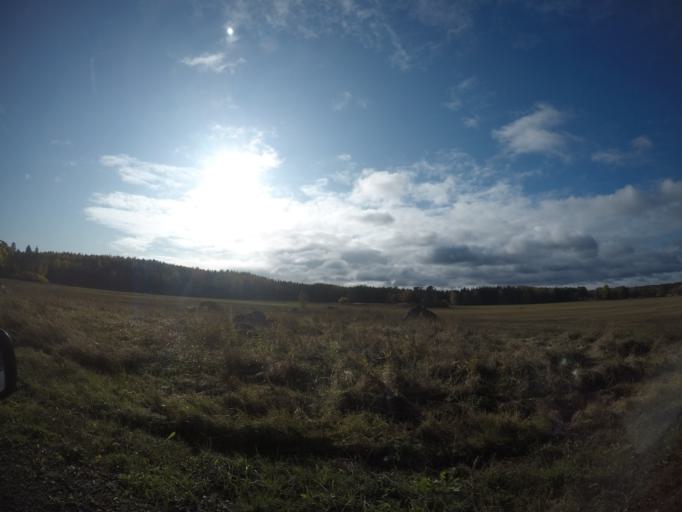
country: SE
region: Soedermanland
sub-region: Eskilstuna Kommun
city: Kvicksund
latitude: 59.3758
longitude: 16.2633
